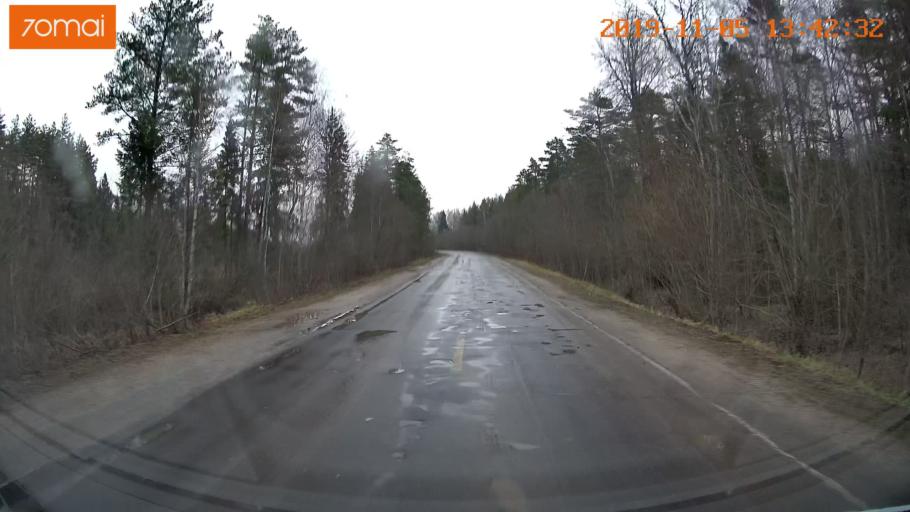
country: RU
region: Ivanovo
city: Shuya
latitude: 56.9672
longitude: 41.3951
